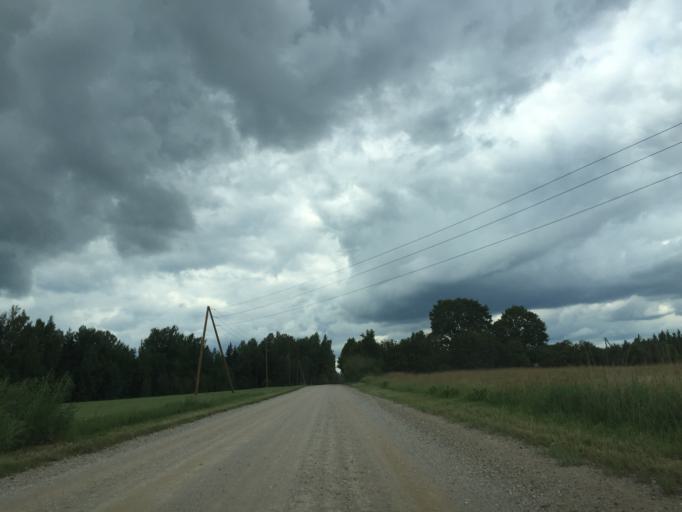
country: LV
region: Malpils
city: Malpils
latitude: 56.8702
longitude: 25.0073
